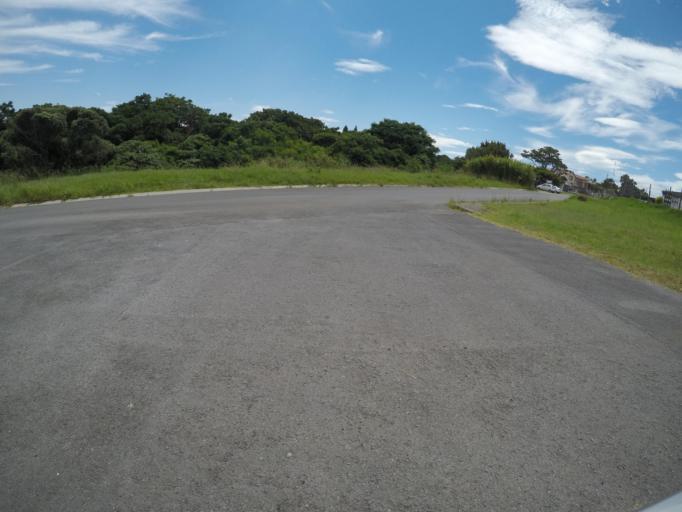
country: ZA
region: Eastern Cape
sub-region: Buffalo City Metropolitan Municipality
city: East London
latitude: -33.0419
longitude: 27.8538
